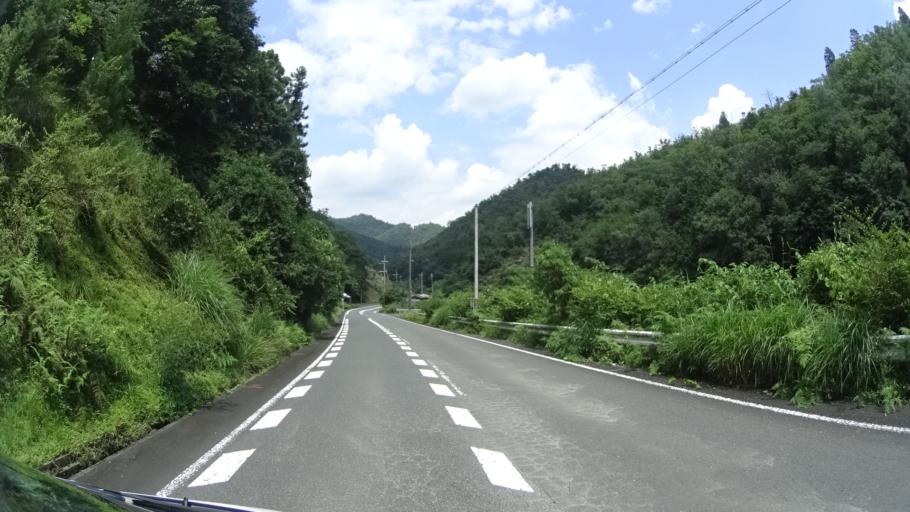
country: JP
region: Hyogo
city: Sasayama
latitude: 35.1817
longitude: 135.2442
